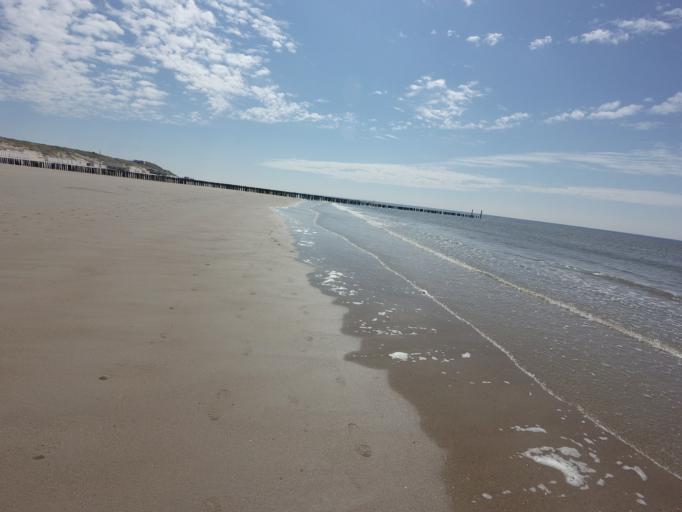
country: NL
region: Zeeland
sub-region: Gemeente Vlissingen
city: Vlissingen
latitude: 51.5151
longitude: 3.4495
